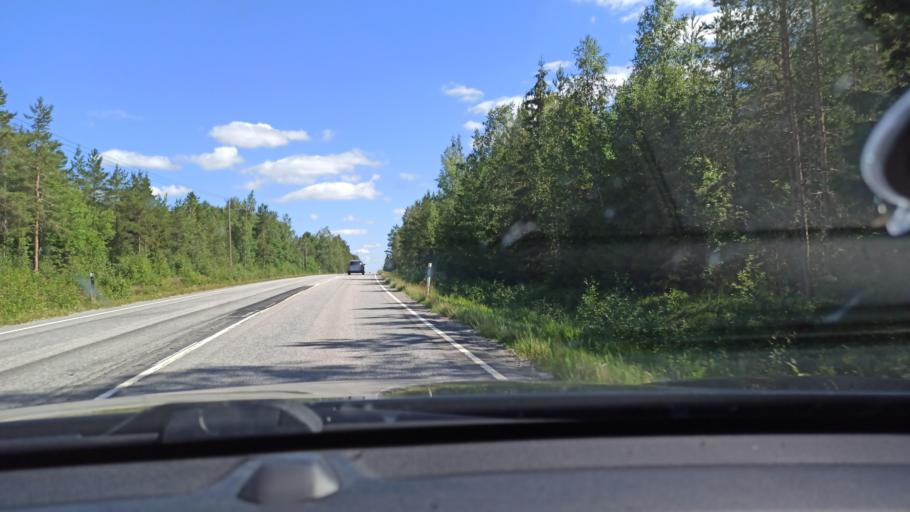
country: FI
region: Ostrobothnia
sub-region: Vaasa
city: Malax
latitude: 62.9717
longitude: 21.5947
